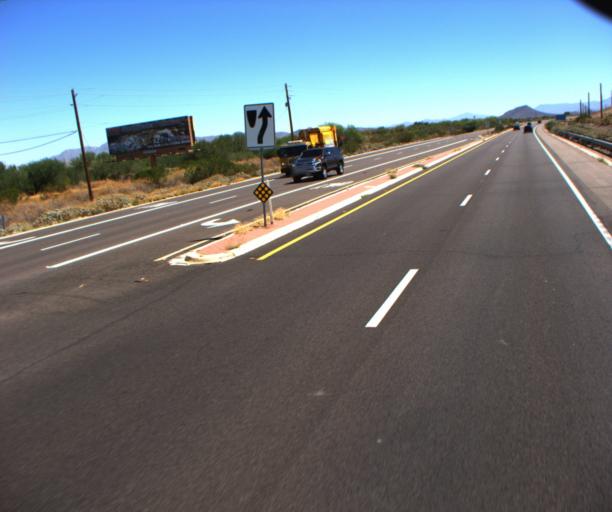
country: US
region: Arizona
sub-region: Maricopa County
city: Mesa
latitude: 33.4727
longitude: -111.8376
